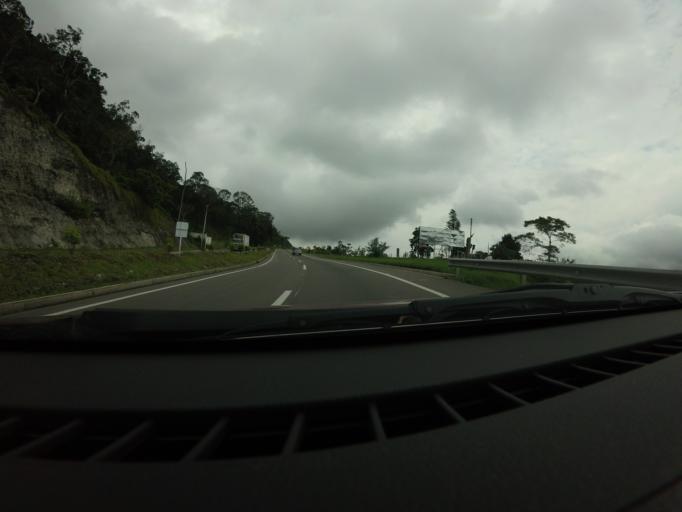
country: CO
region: Cundinamarca
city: San Francisco
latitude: 4.9470
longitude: -74.2940
